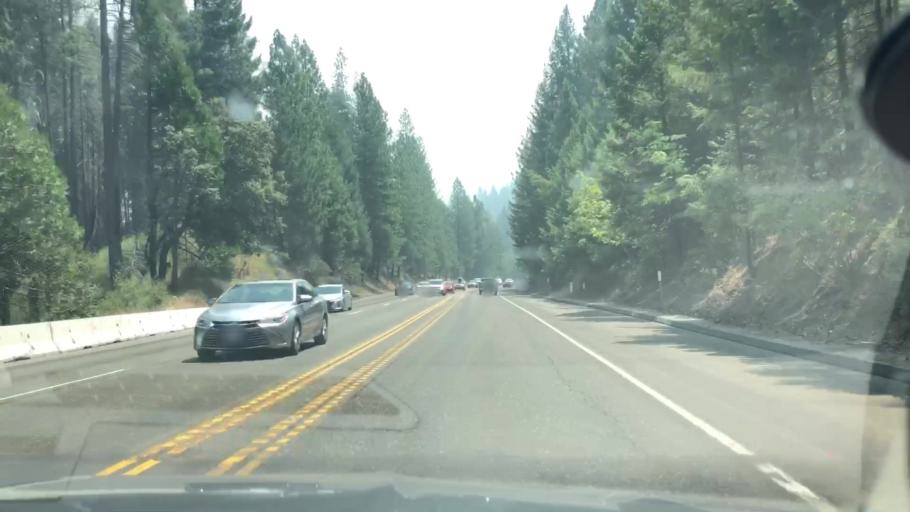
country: US
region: California
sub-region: El Dorado County
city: Pollock Pines
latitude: 38.7622
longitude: -120.5362
